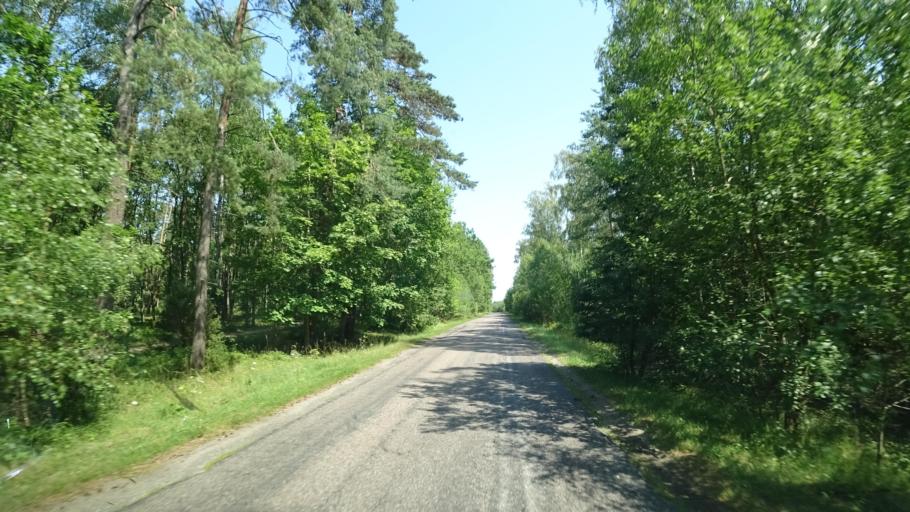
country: PL
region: Pomeranian Voivodeship
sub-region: Powiat chojnicki
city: Brusy
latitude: 53.8726
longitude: 17.6248
